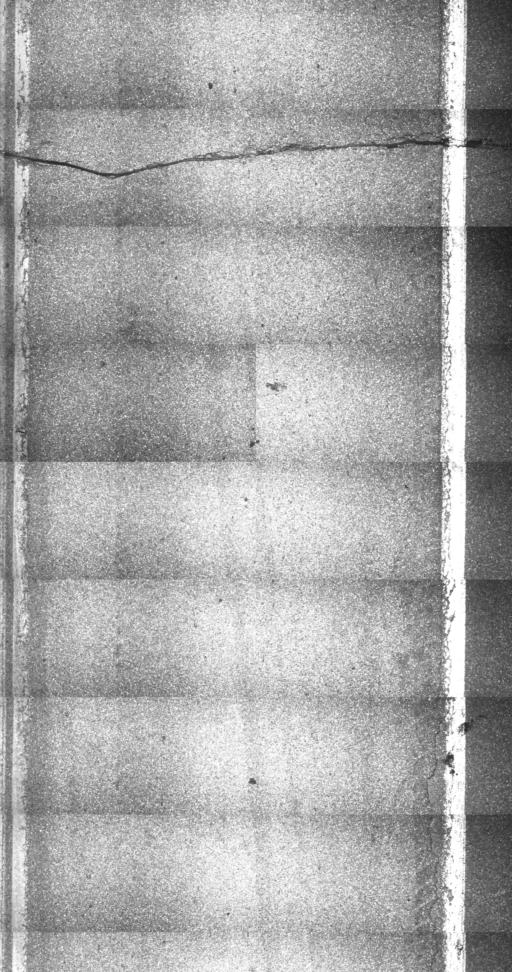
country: US
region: Vermont
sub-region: Chittenden County
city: Colchester
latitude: 44.5284
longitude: -73.1292
